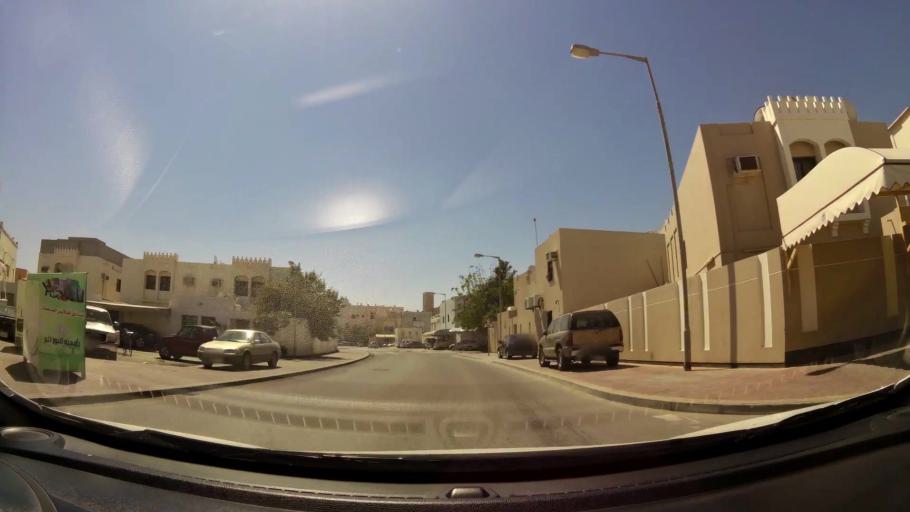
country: BH
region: Muharraq
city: Al Muharraq
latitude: 26.2736
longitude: 50.6089
